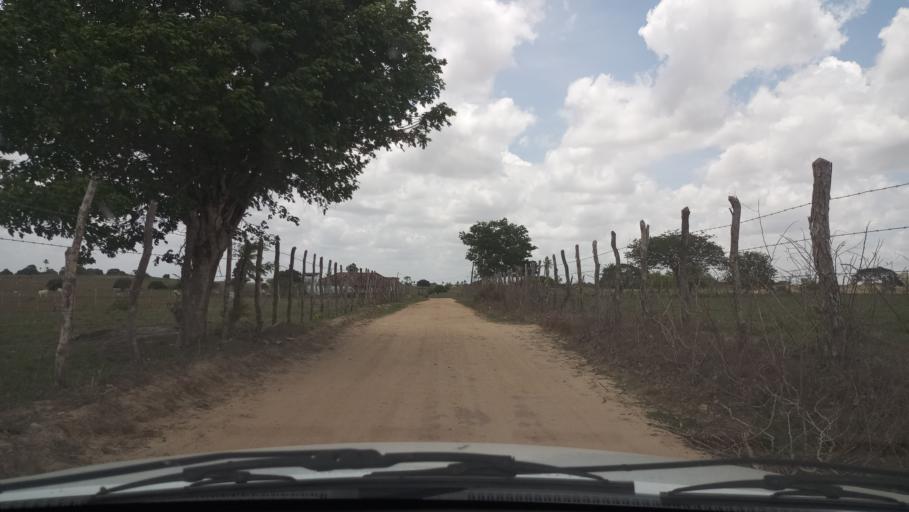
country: BR
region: Rio Grande do Norte
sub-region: Brejinho
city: Brejinho
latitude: -6.2738
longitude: -35.3370
